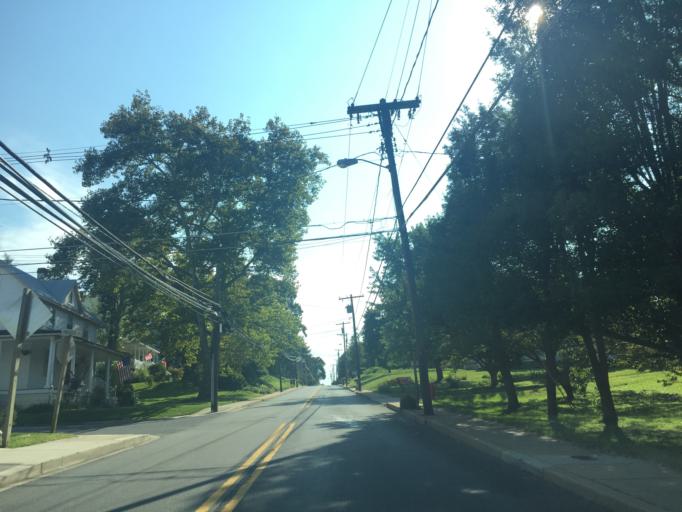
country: US
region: Maryland
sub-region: Carroll County
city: Mount Airy
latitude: 39.3744
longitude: -77.1571
